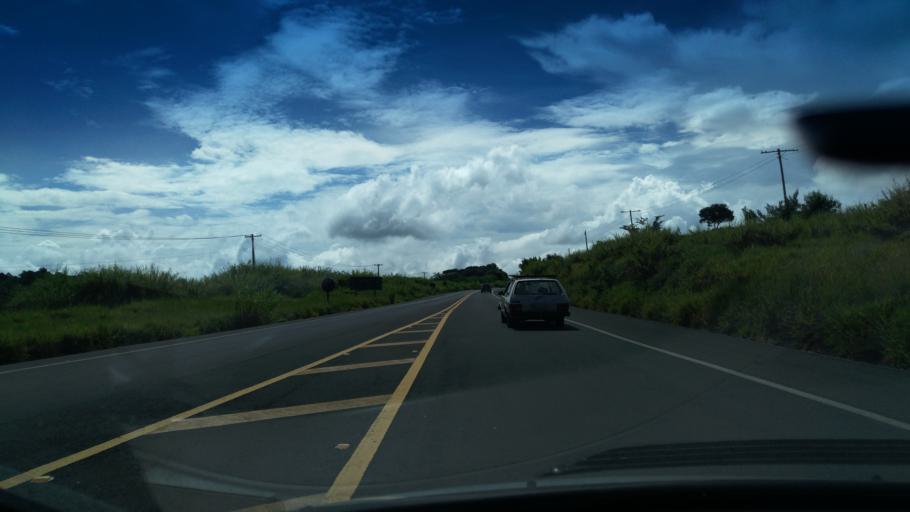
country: BR
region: Sao Paulo
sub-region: Santo Antonio Do Jardim
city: Espirito Santo do Pinhal
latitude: -22.1637
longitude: -46.7352
